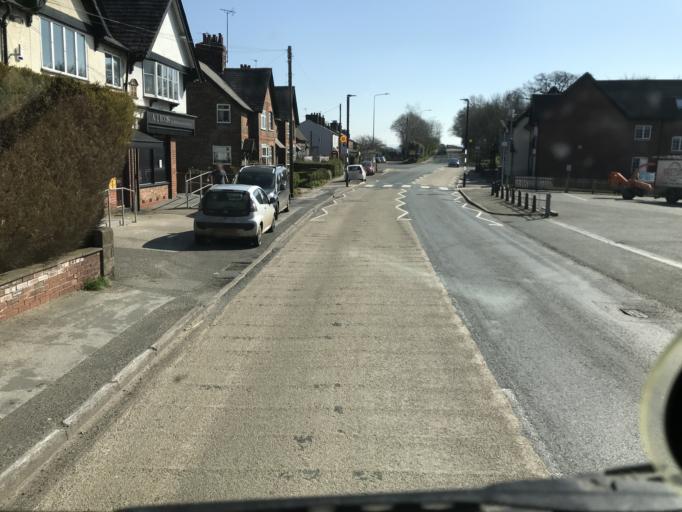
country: GB
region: England
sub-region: Cheshire East
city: Mobberley
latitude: 53.2712
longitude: -2.2840
